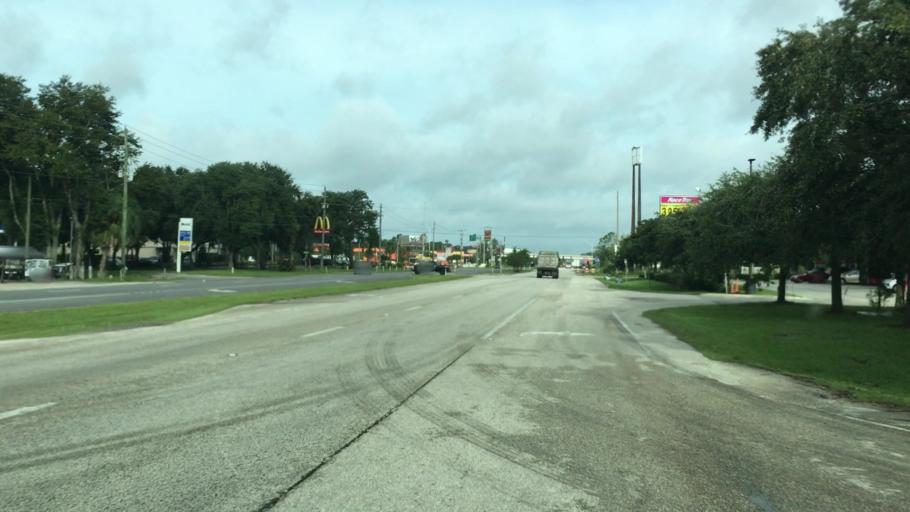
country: US
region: Florida
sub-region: Volusia County
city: Ormond-by-the-Sea
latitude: 29.3328
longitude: -81.1266
